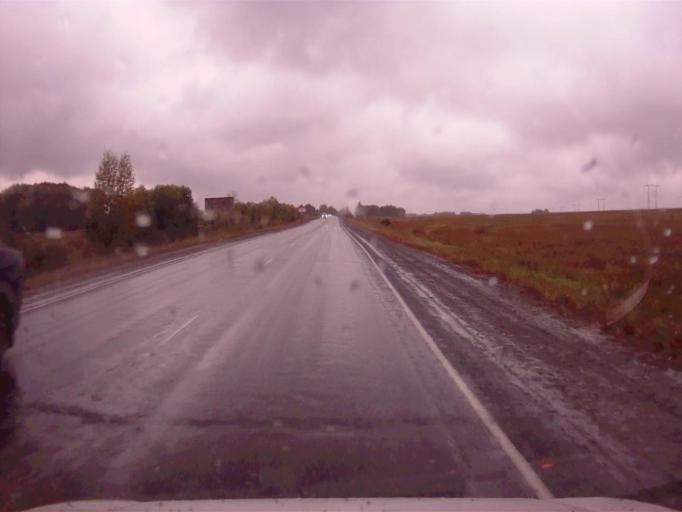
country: RU
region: Chelyabinsk
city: Roshchino
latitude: 55.3931
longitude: 61.1132
